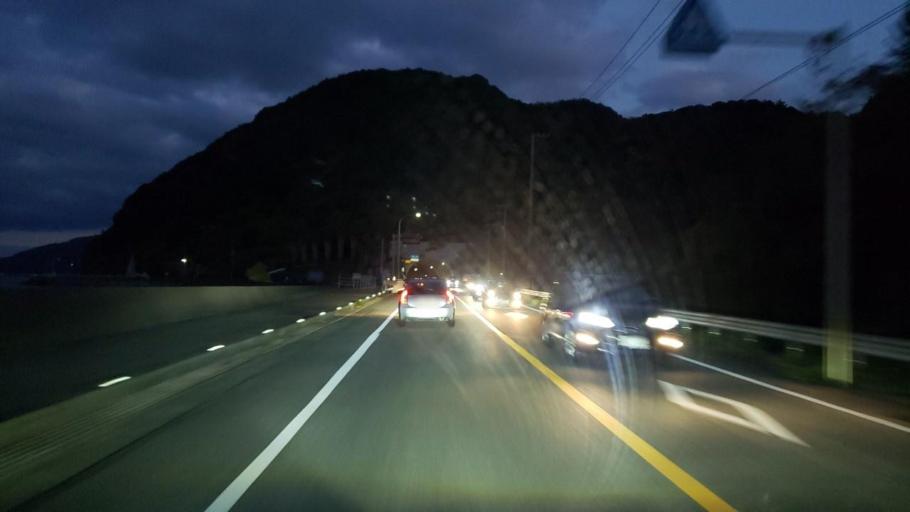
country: JP
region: Tokushima
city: Ishii
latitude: 34.2054
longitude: 134.4517
